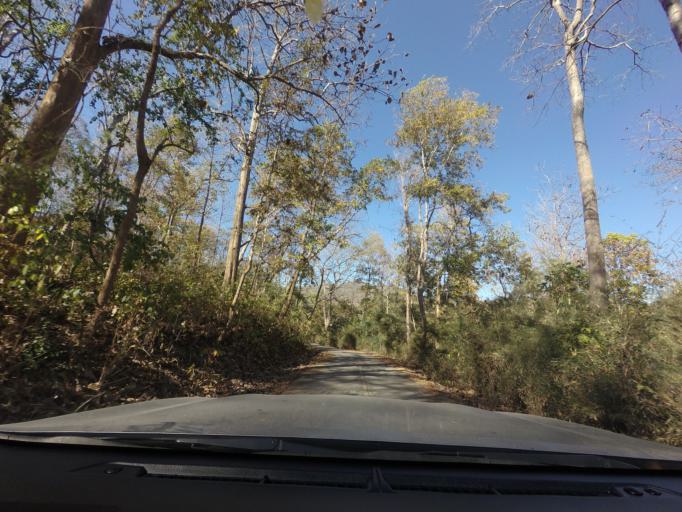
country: TH
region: Mae Hong Son
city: Wiang Nuea
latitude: 19.4021
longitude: 98.4178
